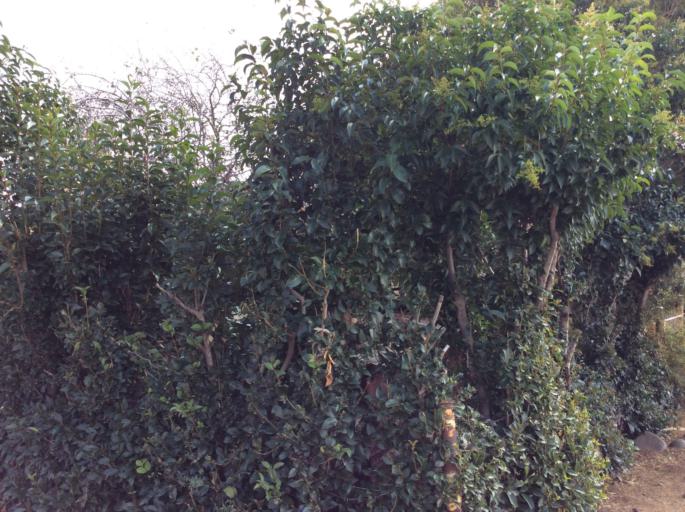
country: LS
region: Mafeteng
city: Mafeteng
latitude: -29.9813
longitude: 27.0059
